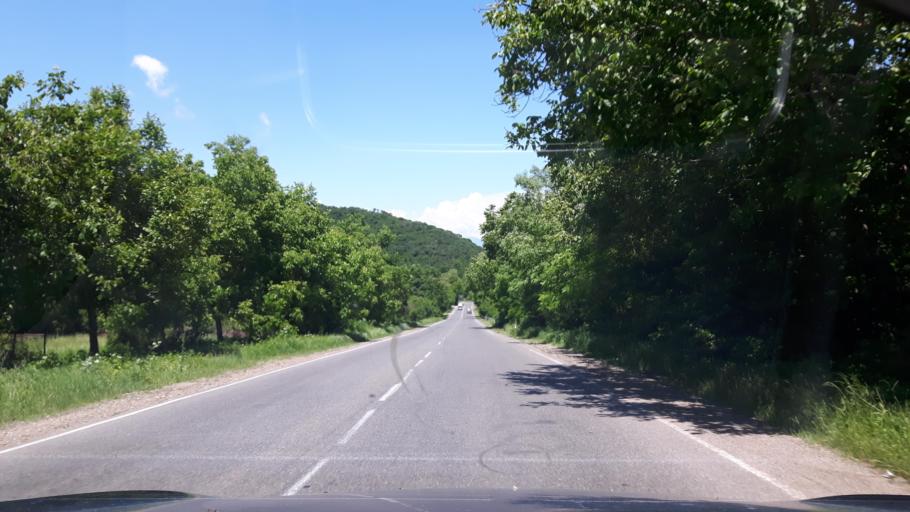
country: GE
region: Kakheti
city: Sighnaghi
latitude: 41.6374
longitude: 45.8266
